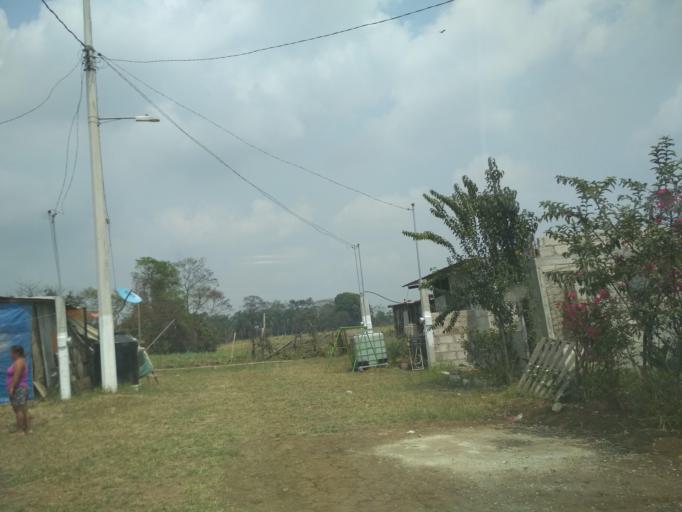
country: MX
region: Veracruz
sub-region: Cordoba
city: Fredepo
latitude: 18.8595
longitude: -96.9830
